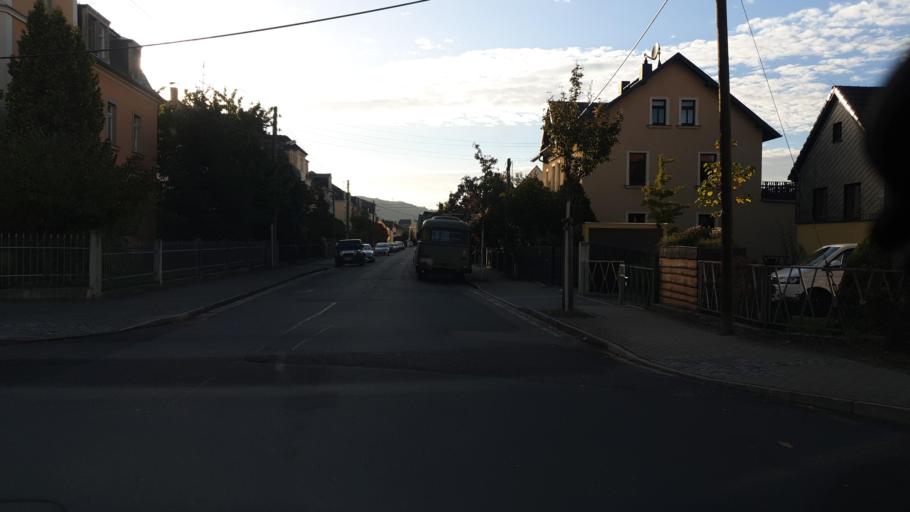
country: DE
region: Saxony
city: Radebeul
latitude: 51.0890
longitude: 13.6349
